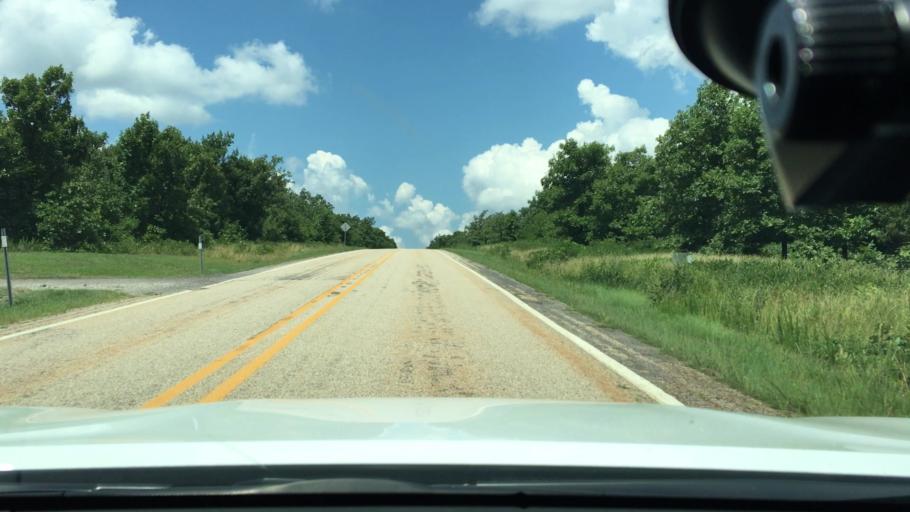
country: US
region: Arkansas
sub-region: Logan County
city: Paris
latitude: 35.1772
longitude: -93.6050
